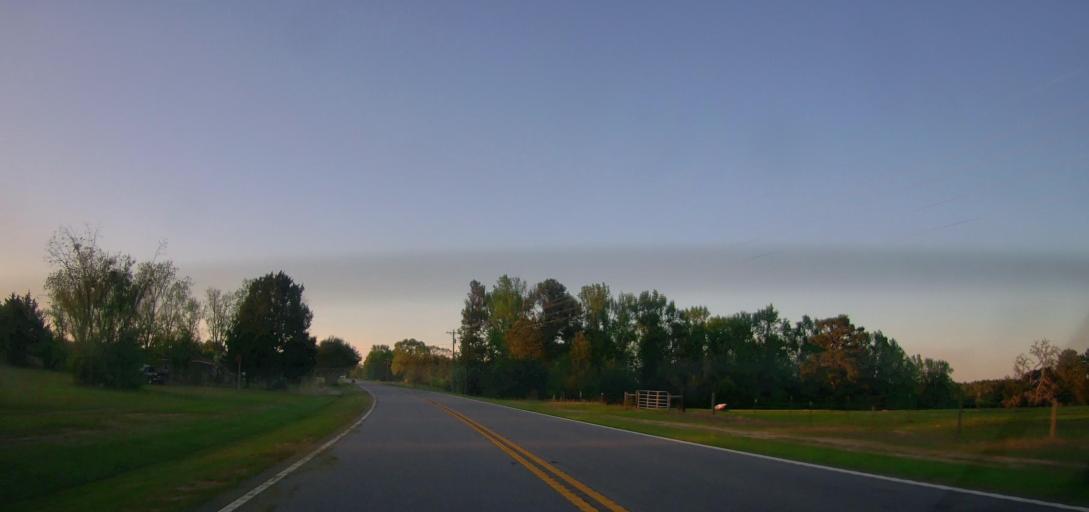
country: US
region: Georgia
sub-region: Marion County
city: Buena Vista
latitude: 32.4700
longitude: -84.6357
